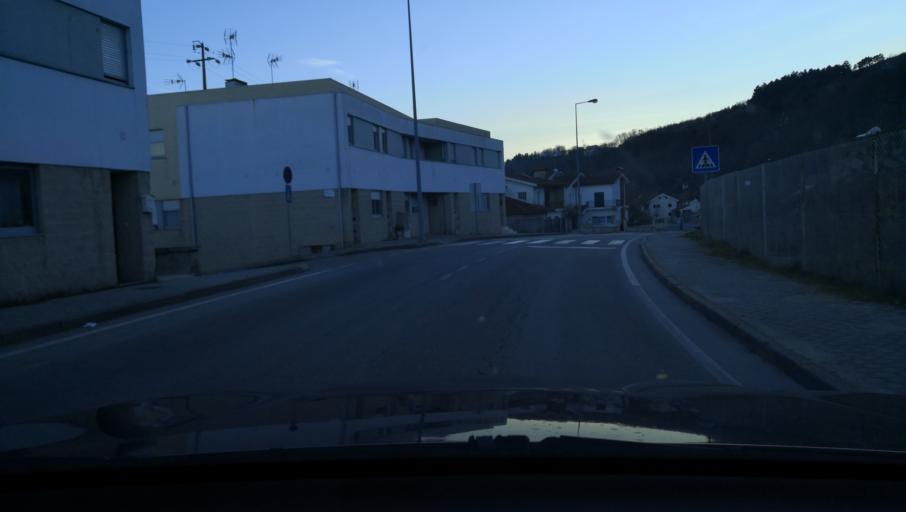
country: PT
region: Vila Real
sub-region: Vila Pouca de Aguiar
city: Vila Pouca de Aguiar
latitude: 41.4987
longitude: -7.6474
